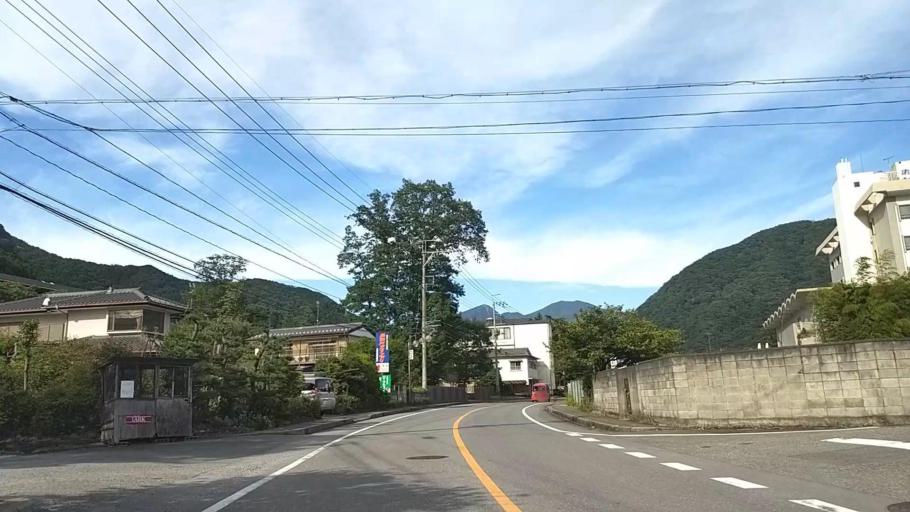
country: JP
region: Tochigi
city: Imaichi
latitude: 36.8221
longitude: 139.7101
